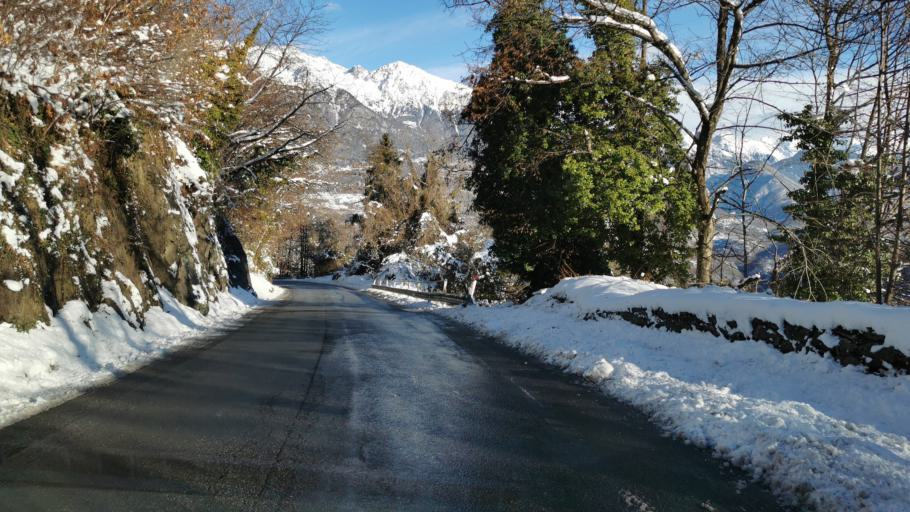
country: IT
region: Lombardy
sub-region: Provincia di Sondrio
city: Bema
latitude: 46.1190
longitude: 9.5609
